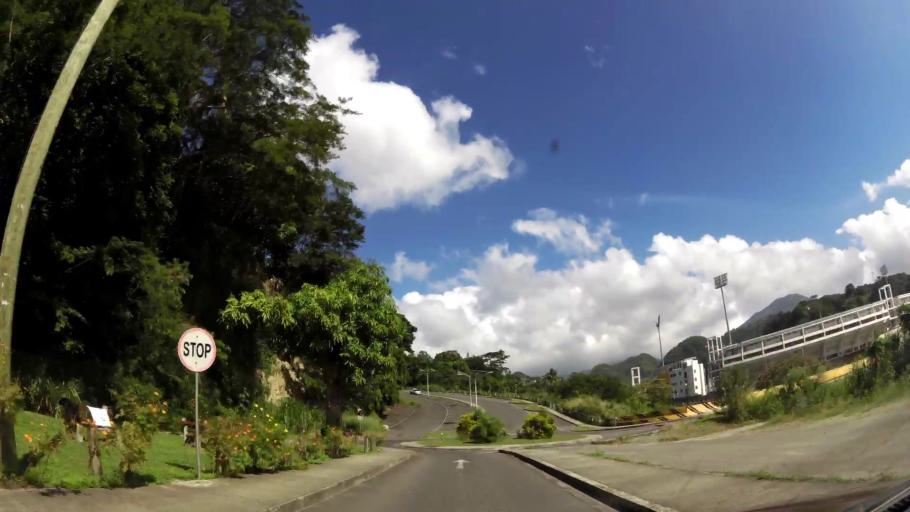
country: DM
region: Saint George
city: Roseau
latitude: 15.3027
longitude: -61.3868
